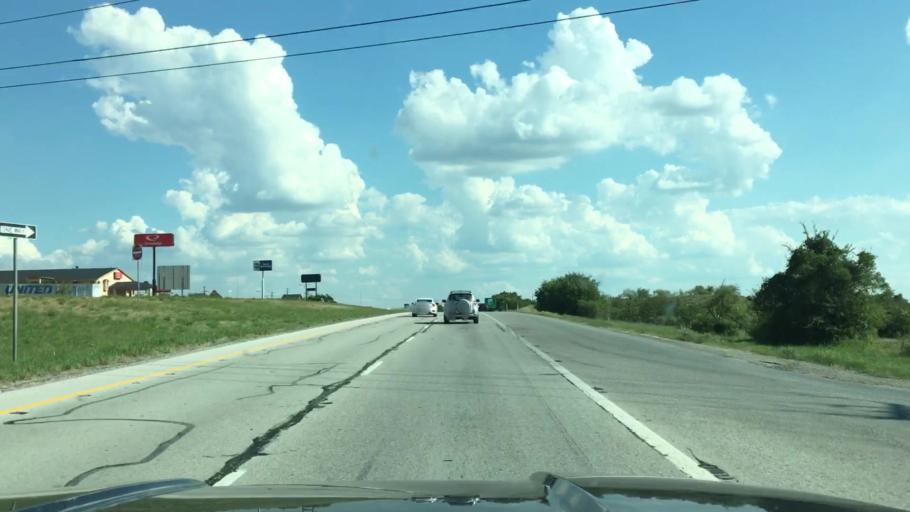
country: US
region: Texas
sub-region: Wise County
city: Decatur
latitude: 33.2215
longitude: -97.5900
